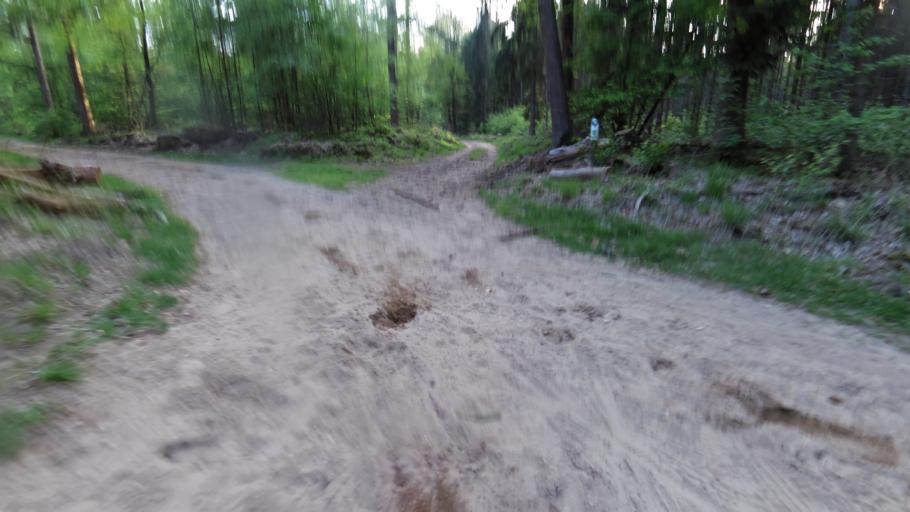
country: NL
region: Gelderland
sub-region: Gemeente Ede
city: Ede
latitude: 52.0605
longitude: 5.6775
